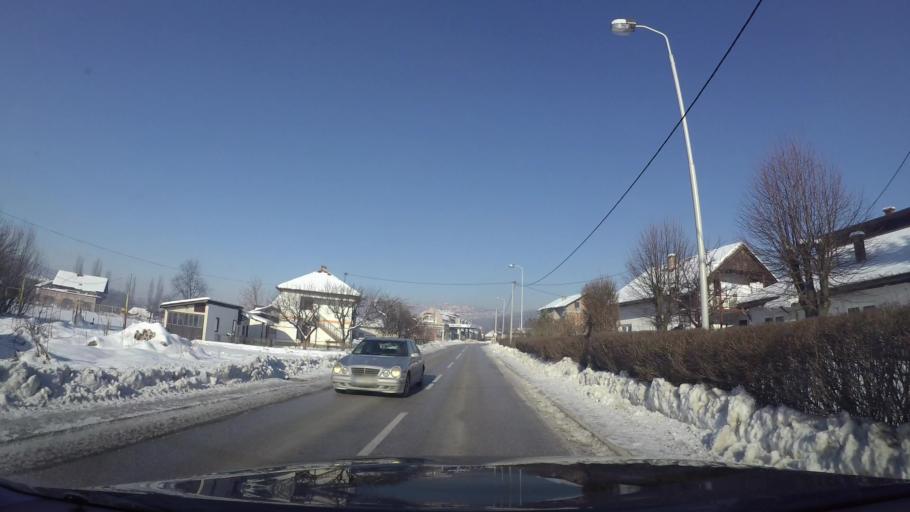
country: BA
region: Federation of Bosnia and Herzegovina
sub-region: Kanton Sarajevo
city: Sarajevo
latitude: 43.8259
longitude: 18.3740
